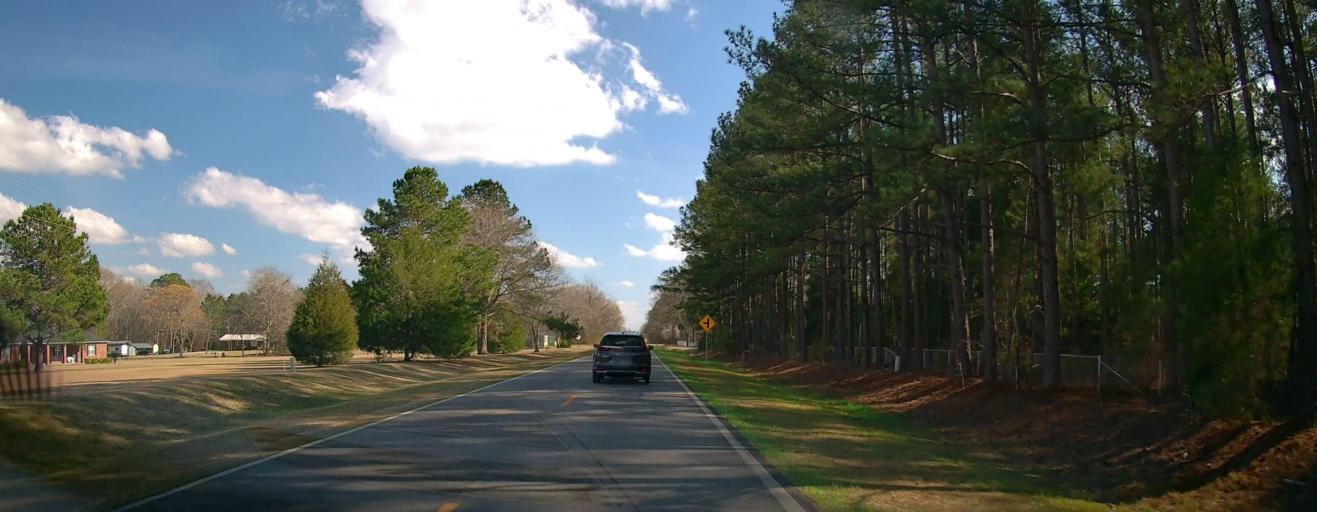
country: US
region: Georgia
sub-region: Laurens County
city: Dublin
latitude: 32.6124
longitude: -83.0818
